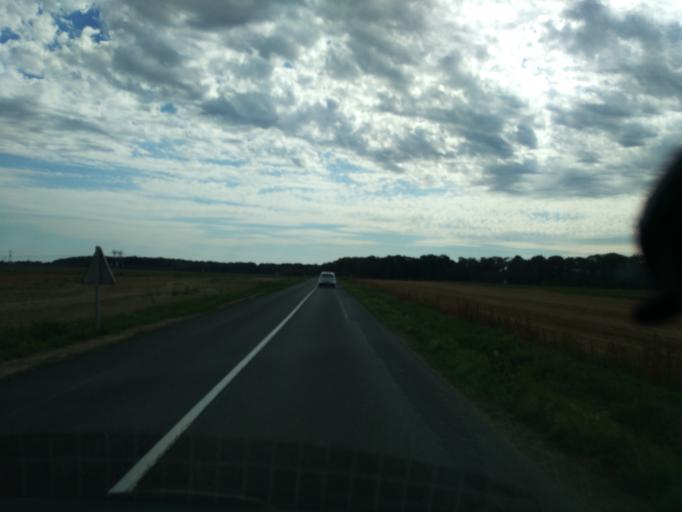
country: FR
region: Ile-de-France
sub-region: Departement de l'Essonne
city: Briis-sous-Forges
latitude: 48.6455
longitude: 2.1206
